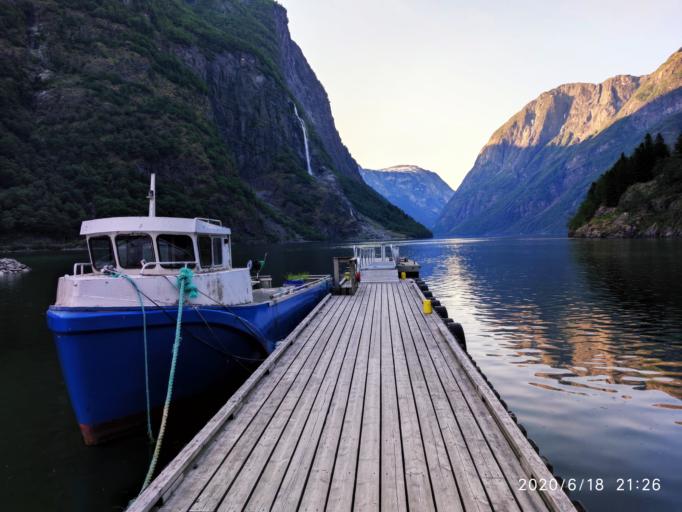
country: NO
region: Sogn og Fjordane
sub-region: Leikanger
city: Hermansverk
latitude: 60.8801
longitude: 6.8440
